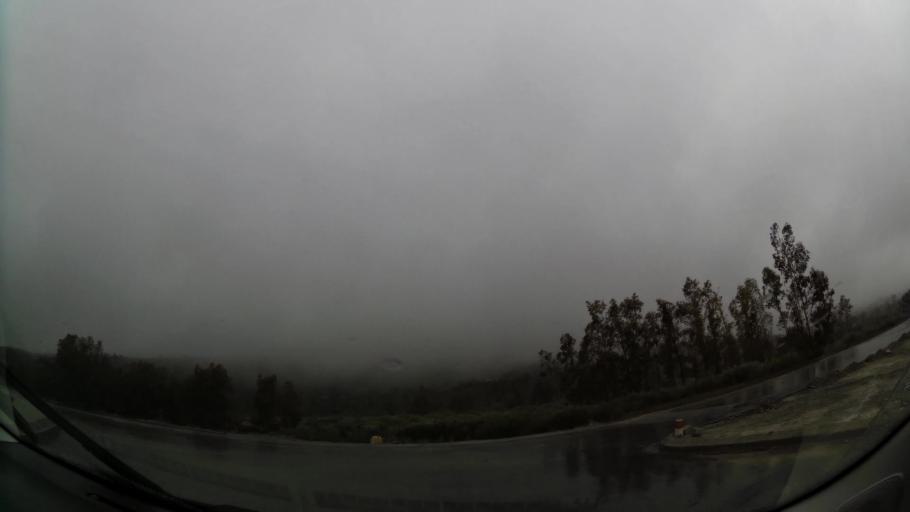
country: MA
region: Taza-Al Hoceima-Taounate
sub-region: Taza
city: Aknoul
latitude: 34.8020
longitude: -3.7403
